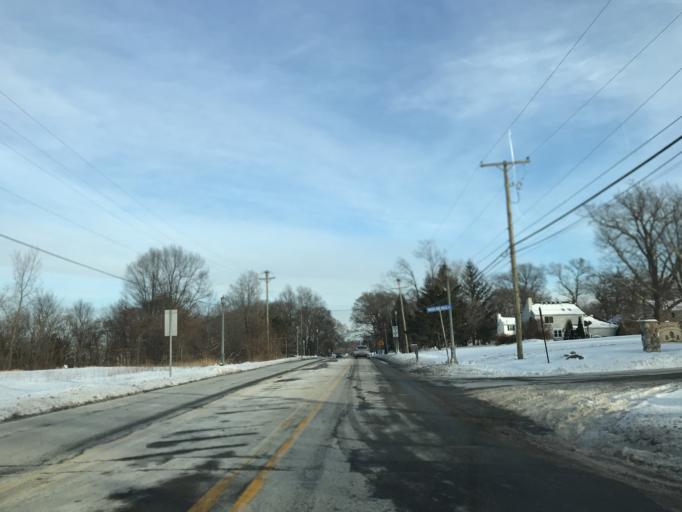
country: US
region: Michigan
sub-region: Oakland County
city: Walled Lake
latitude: 42.5327
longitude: -83.4984
